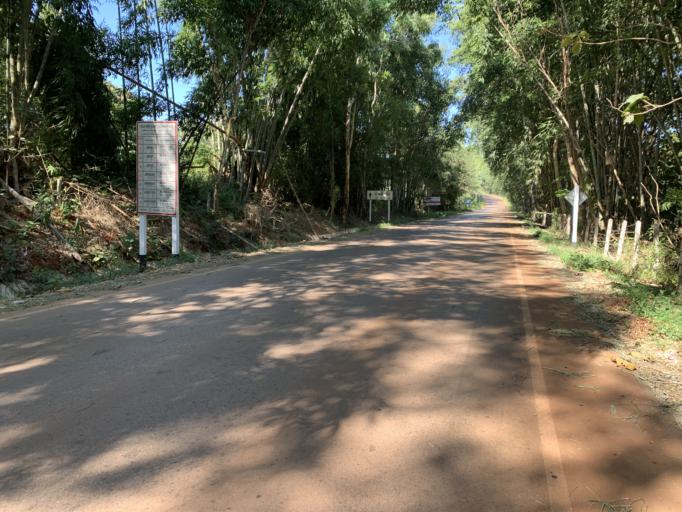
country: TH
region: Tak
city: Phop Phra
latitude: 16.4880
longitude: 98.7869
